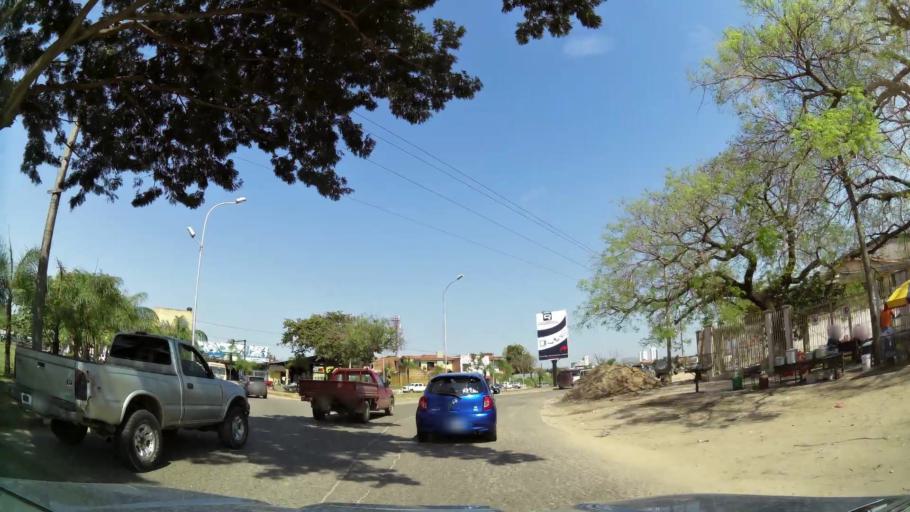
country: BO
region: Santa Cruz
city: Santa Cruz de la Sierra
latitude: -17.7493
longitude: -63.1812
